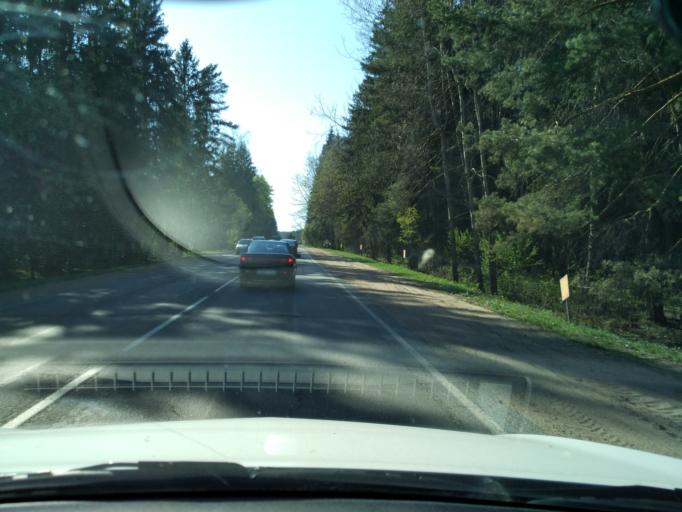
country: BY
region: Minsk
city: Lyeskawka
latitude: 53.9603
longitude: 27.7157
